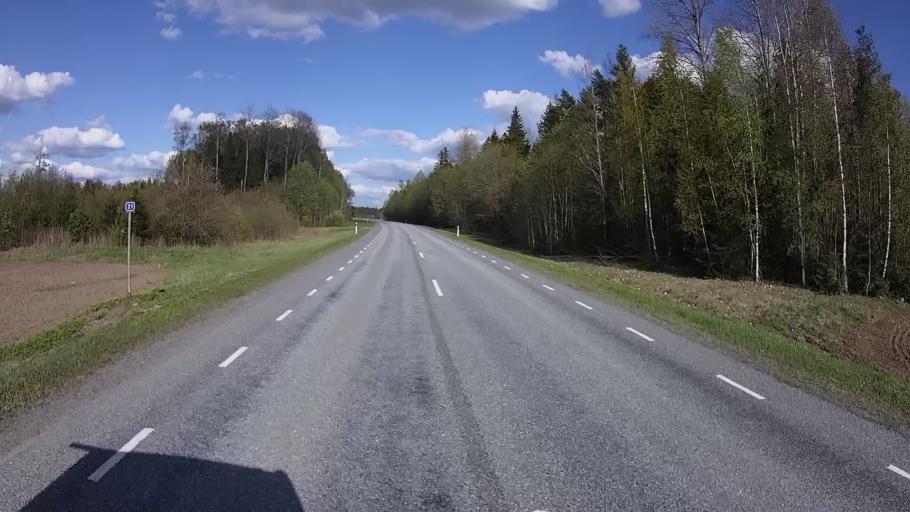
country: EE
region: Jogevamaa
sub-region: Poltsamaa linn
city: Poltsamaa
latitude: 58.6785
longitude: 26.0440
